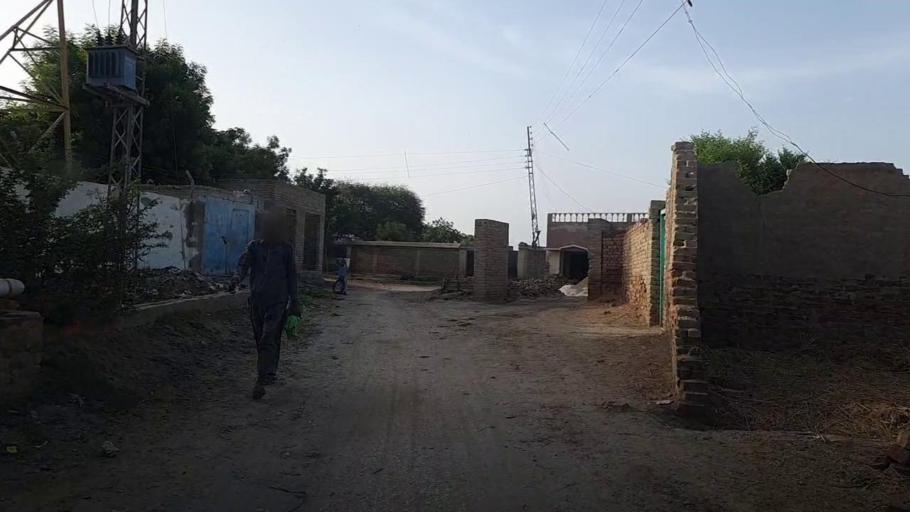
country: PK
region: Sindh
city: Bhiria
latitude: 26.9108
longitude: 68.2638
